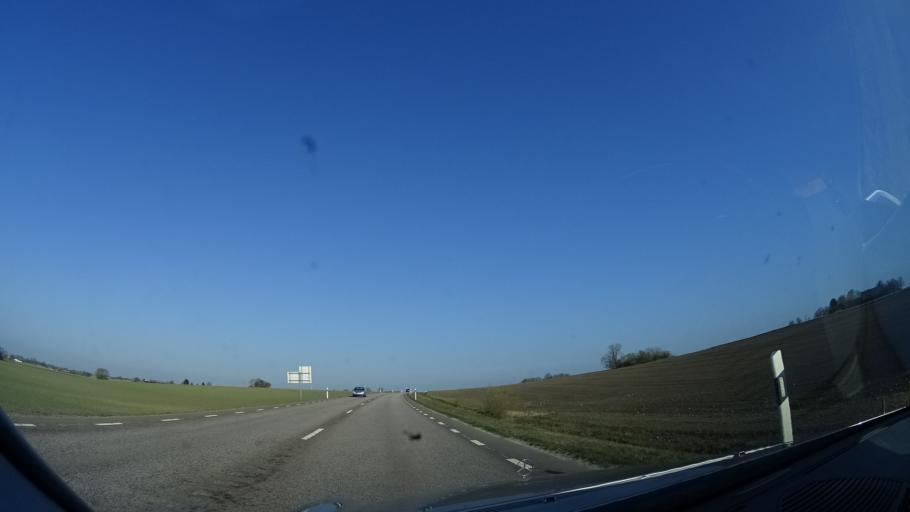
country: SE
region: Skane
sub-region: Svalovs Kommun
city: Svaloev
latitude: 55.8699
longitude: 13.1847
